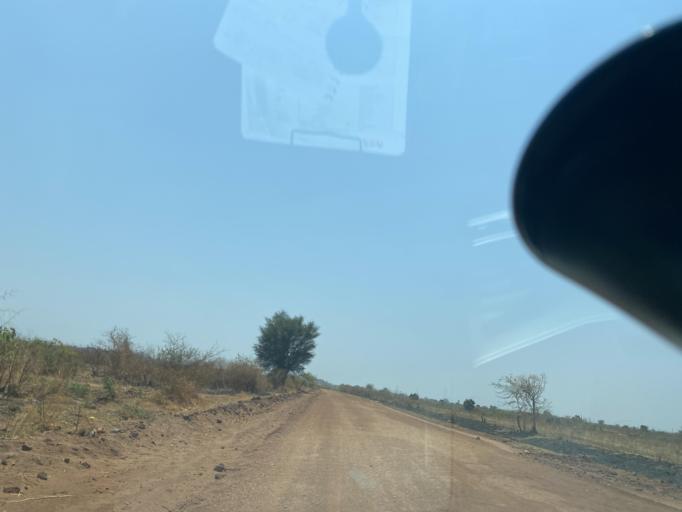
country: ZM
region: Lusaka
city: Lusaka
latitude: -15.4625
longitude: 27.9121
